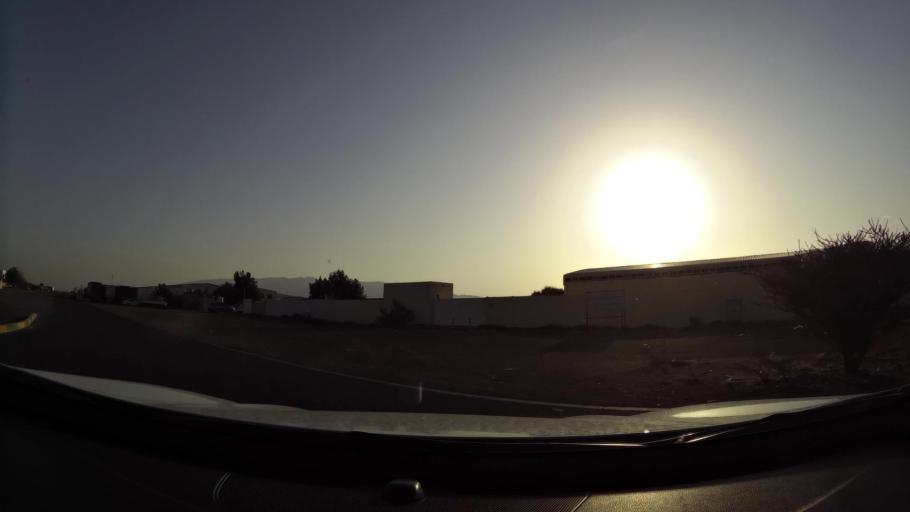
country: AE
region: Abu Dhabi
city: Al Ain
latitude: 24.1480
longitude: 55.8337
